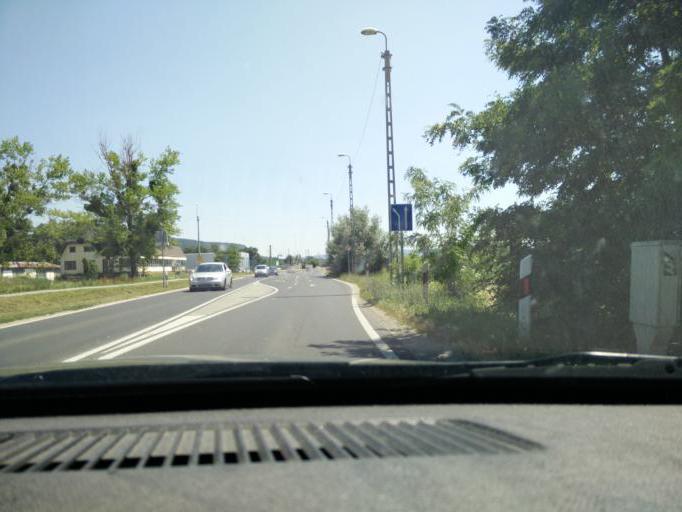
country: HU
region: Komarom-Esztergom
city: Vertesszolos
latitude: 47.6132
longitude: 18.3822
